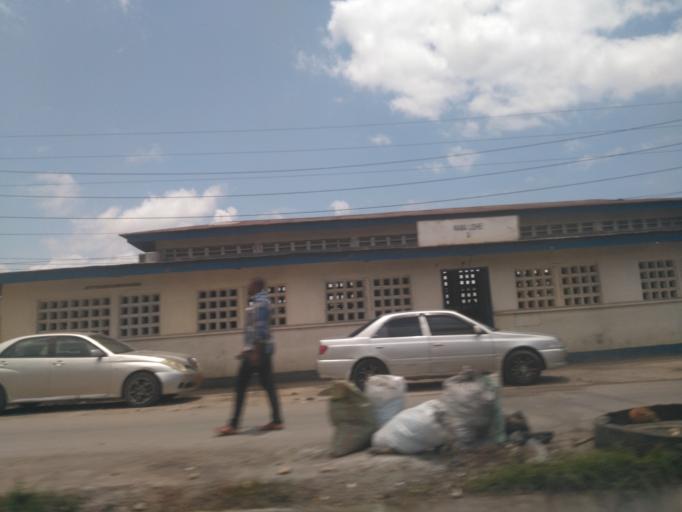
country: TZ
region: Dar es Salaam
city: Dar es Salaam
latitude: -6.8444
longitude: 39.2934
